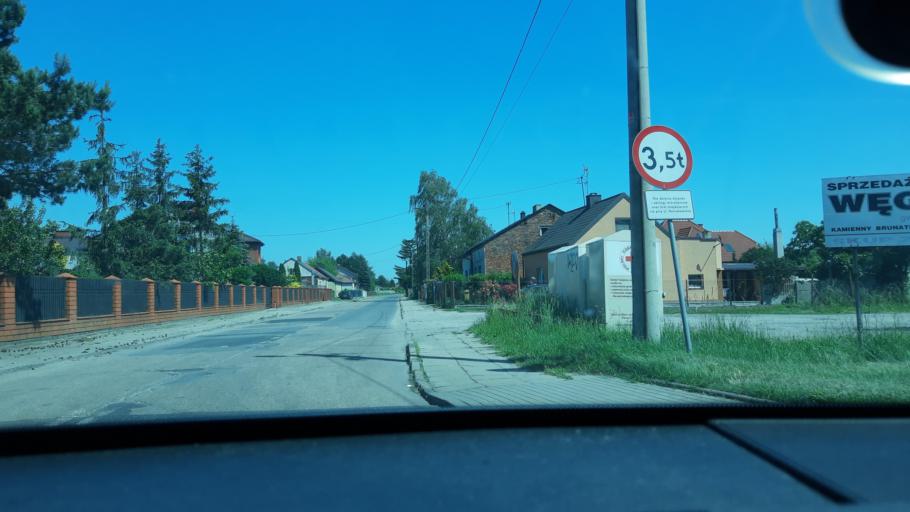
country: PL
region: Lodz Voivodeship
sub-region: Powiat zdunskowolski
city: Zdunska Wola
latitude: 51.6116
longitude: 18.9655
